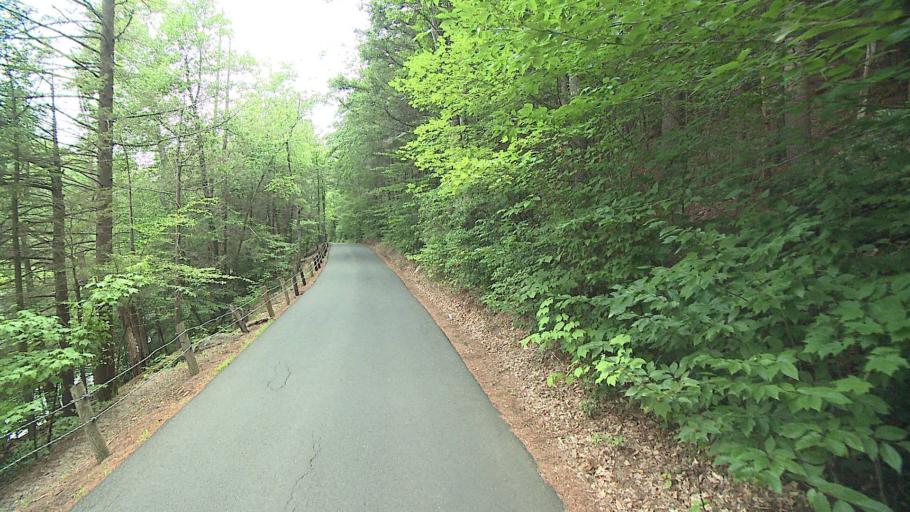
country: US
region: Connecticut
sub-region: Litchfield County
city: Winsted
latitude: 41.9492
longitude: -73.0140
